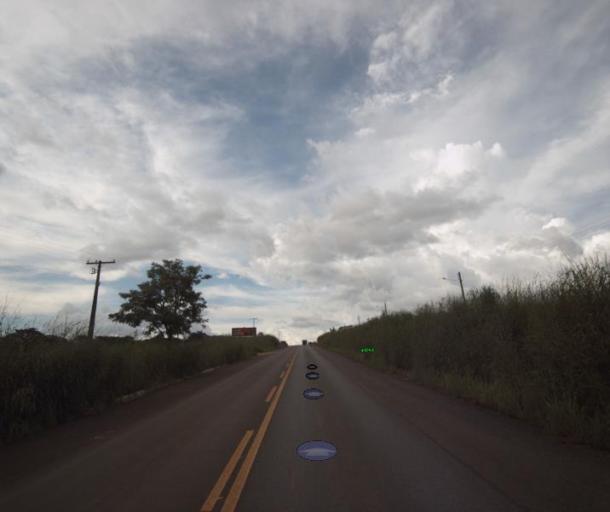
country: BR
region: Goias
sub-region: Niquelandia
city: Niquelandia
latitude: -14.4768
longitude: -48.4888
